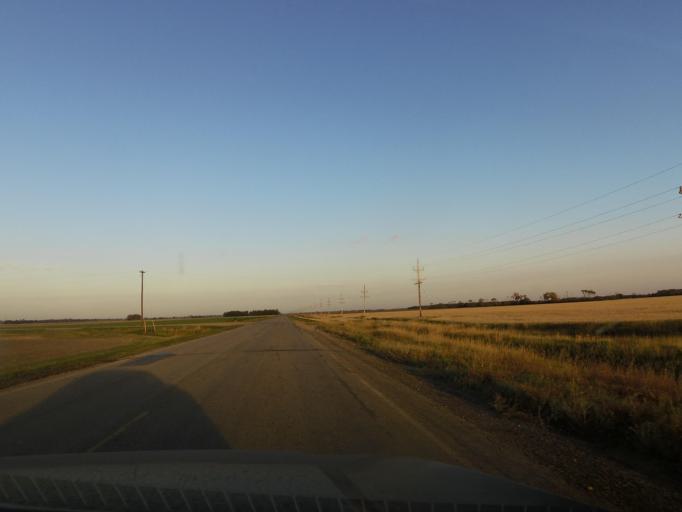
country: CA
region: Manitoba
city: Altona
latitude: 48.9634
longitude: -97.6084
